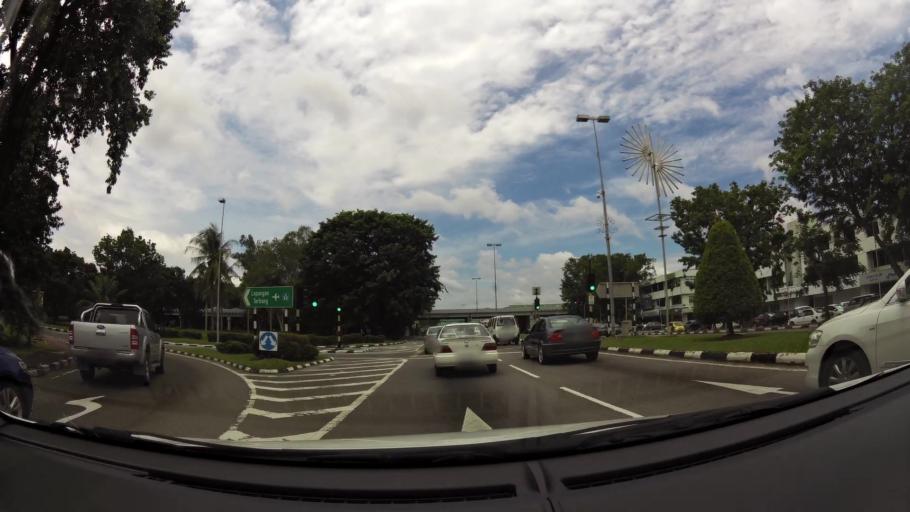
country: BN
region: Brunei and Muara
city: Bandar Seri Begawan
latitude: 4.9100
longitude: 114.9197
